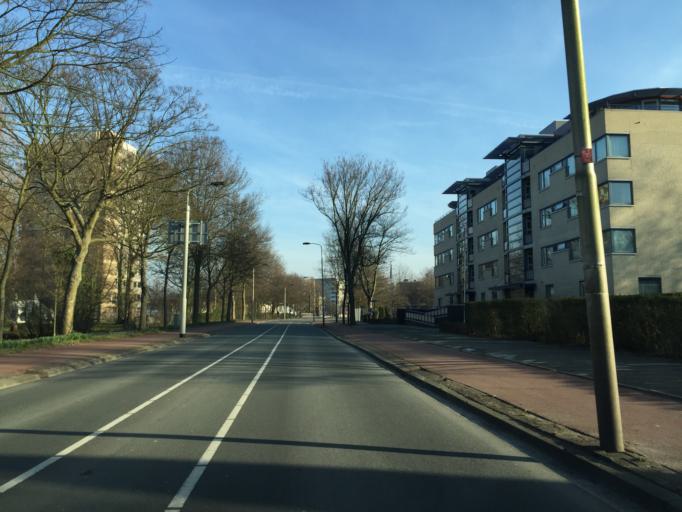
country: NL
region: South Holland
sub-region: Gemeente Delft
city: Delft
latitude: 52.0204
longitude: 4.3600
